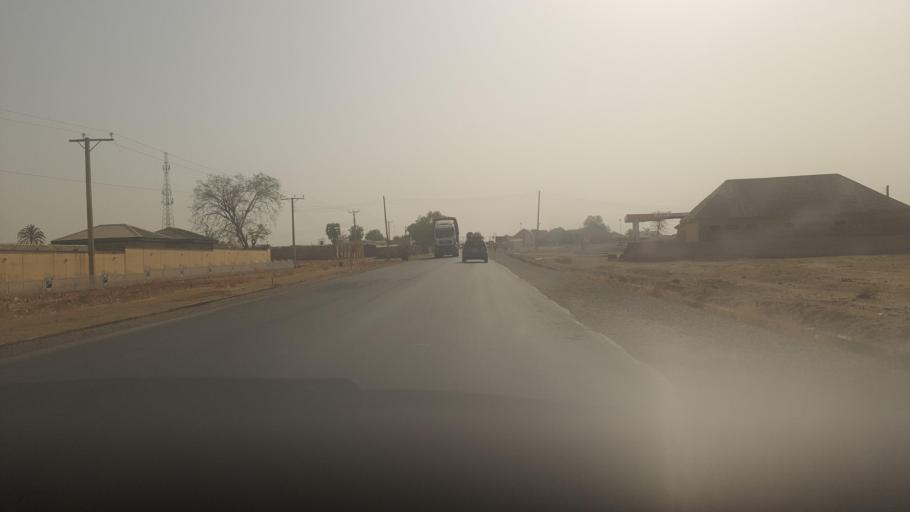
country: NG
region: Bauchi
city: Dindima
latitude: 10.2628
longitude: 9.9997
